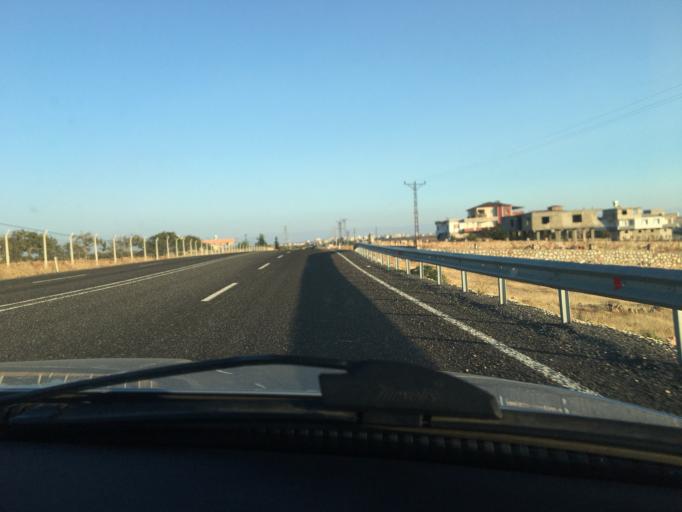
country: TR
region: Sanliurfa
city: Halfeti
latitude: 37.2433
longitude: 37.9022
